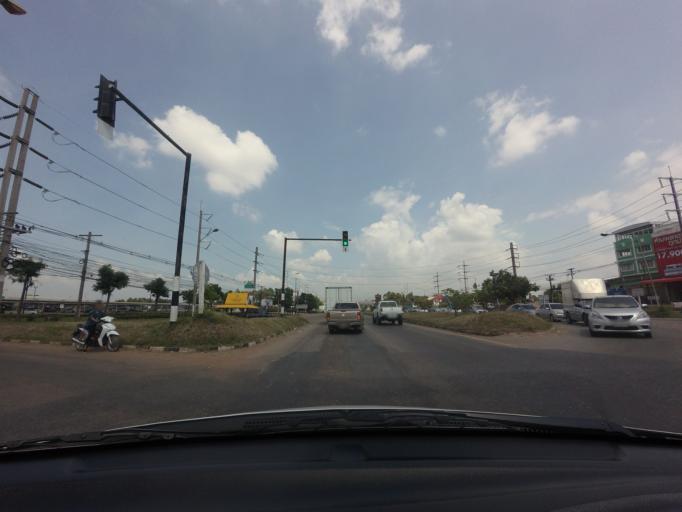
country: TH
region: Prachin Buri
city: Si Maha Phot
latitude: 13.8937
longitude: 101.5796
